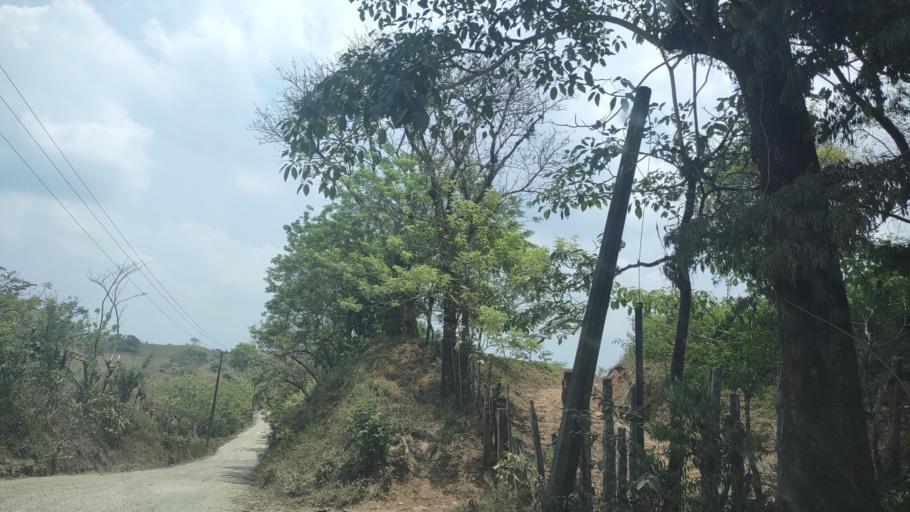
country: MX
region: Tabasco
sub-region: Huimanguillo
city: Francisco Rueda
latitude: 17.6480
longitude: -93.9057
